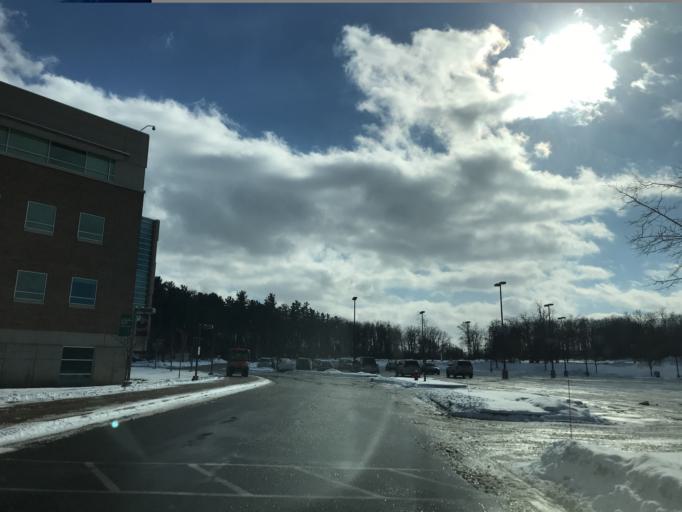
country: US
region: Michigan
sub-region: Washtenaw County
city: Ypsilanti
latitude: 42.2636
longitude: -83.6681
